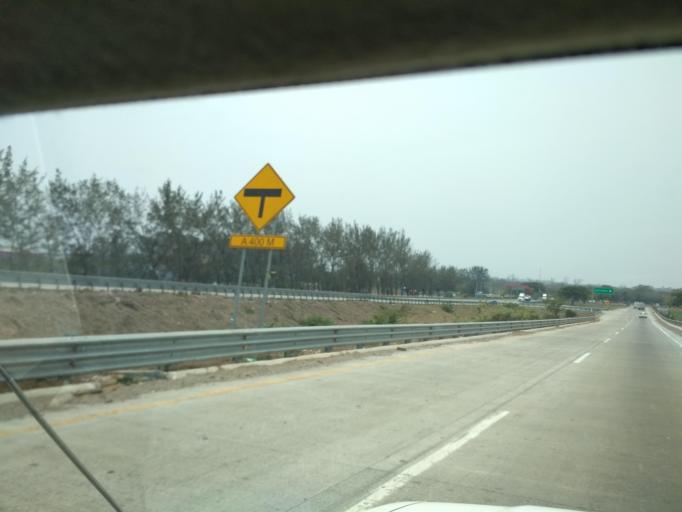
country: MX
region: Veracruz
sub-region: Veracruz
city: Oasis
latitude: 19.1827
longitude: -96.2475
